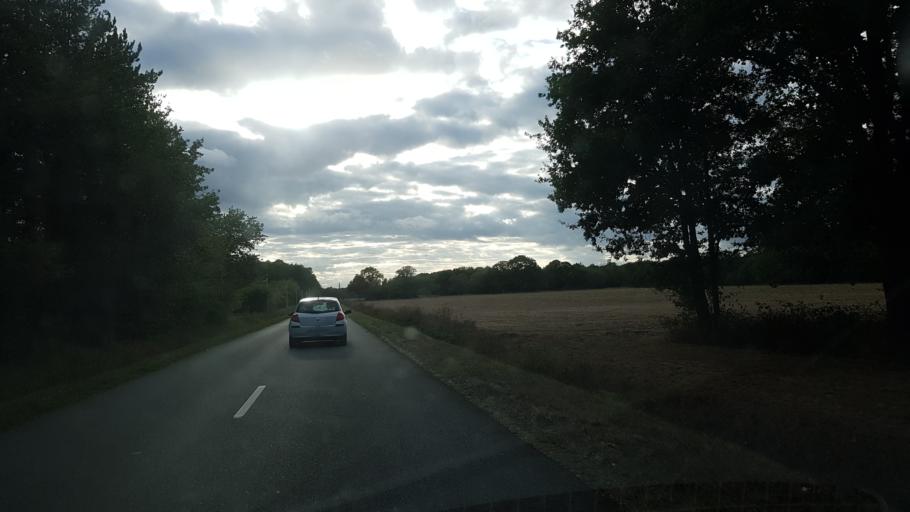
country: FR
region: Centre
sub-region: Departement du Loiret
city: Cerdon
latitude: 47.7021
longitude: 2.3047
